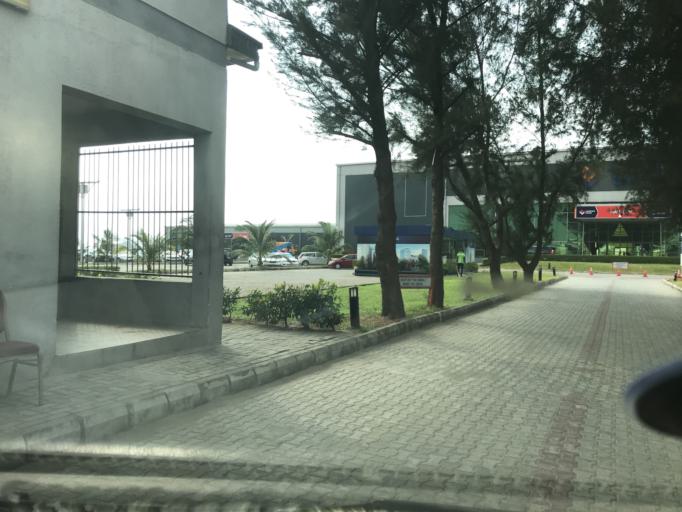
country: NG
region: Lagos
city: Ikoyi
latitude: 6.4238
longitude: 3.4451
